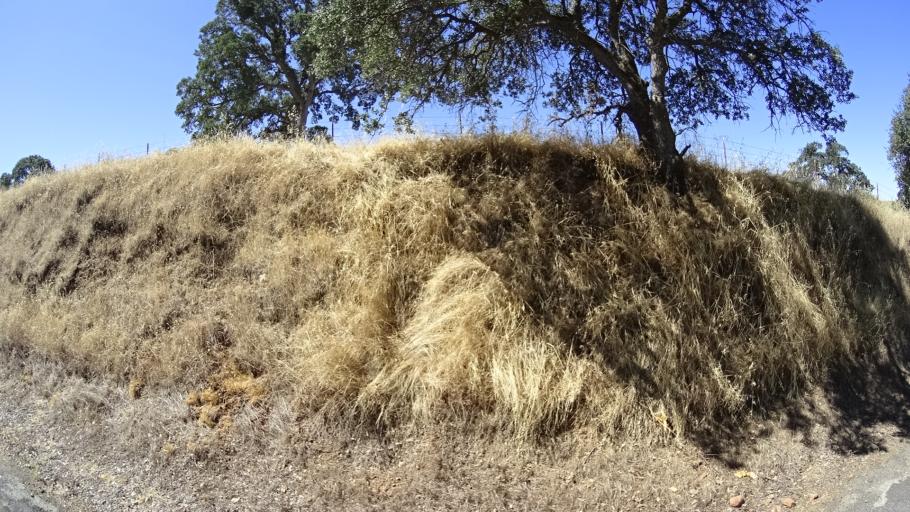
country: US
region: California
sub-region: Calaveras County
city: Rancho Calaveras
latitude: 38.0147
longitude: -120.8132
